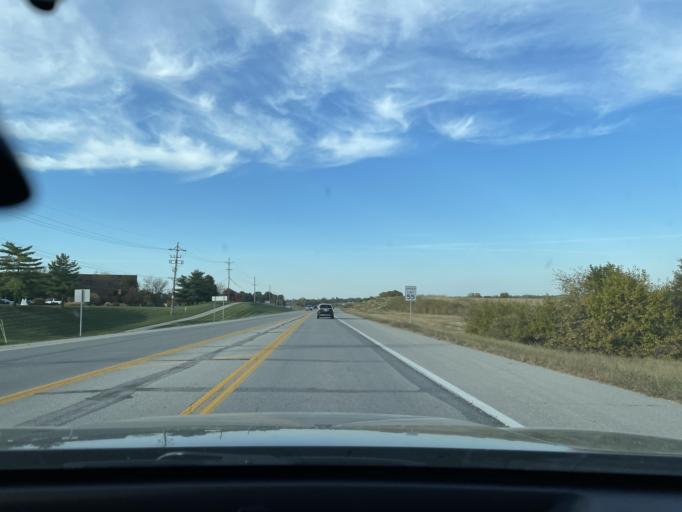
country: US
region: Missouri
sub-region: Buchanan County
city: Saint Joseph
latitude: 39.7711
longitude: -94.7682
